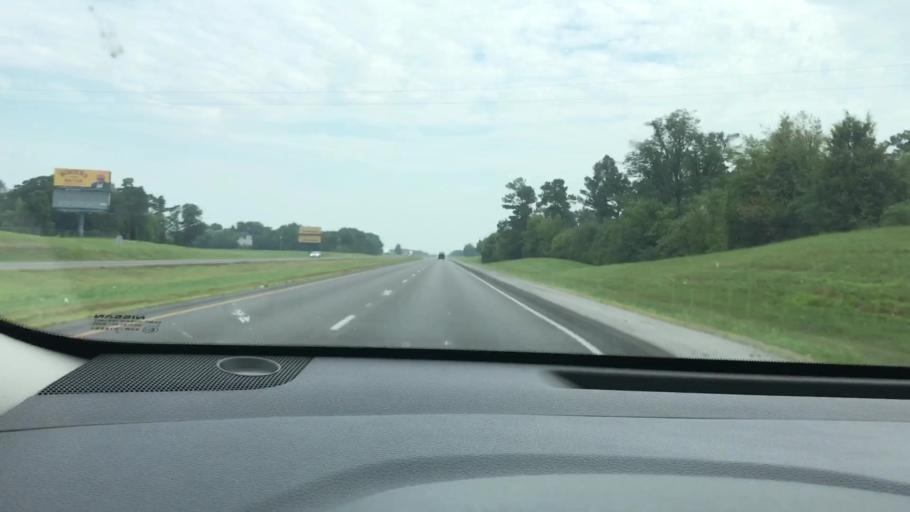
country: US
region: Kentucky
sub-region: Calloway County
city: Murray
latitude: 36.6794
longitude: -88.3026
